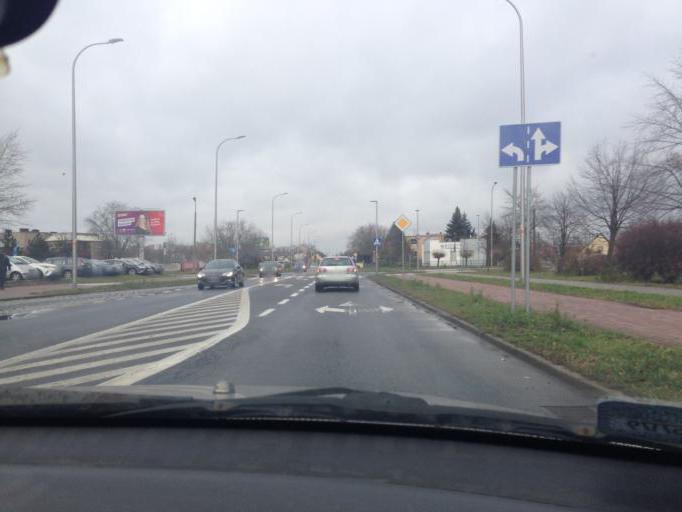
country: PL
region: Opole Voivodeship
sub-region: Powiat opolski
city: Opole
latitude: 50.6753
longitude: 17.9603
